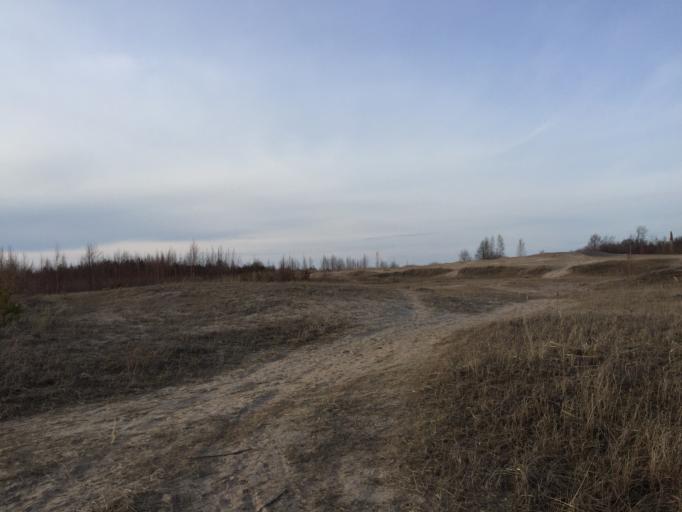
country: LV
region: Salacgrivas
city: Ainazi
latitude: 57.8686
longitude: 24.3560
